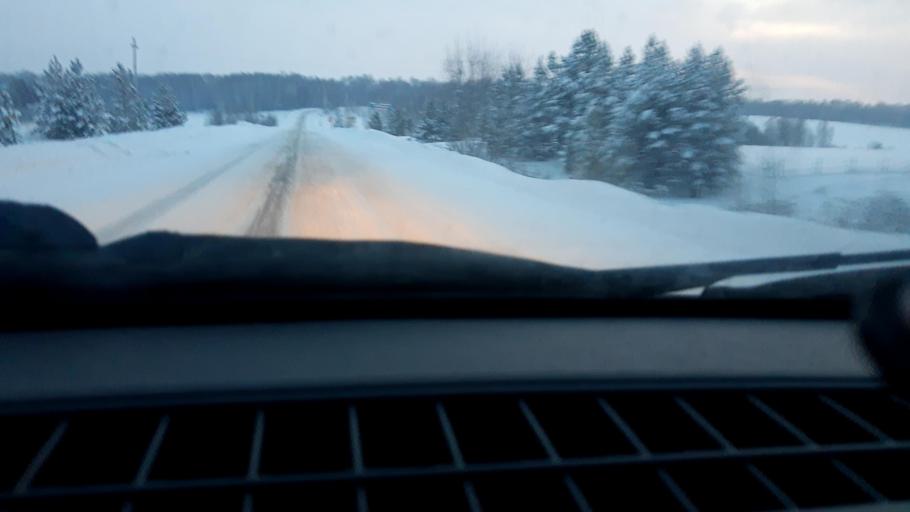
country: RU
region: Bashkortostan
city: Davlekanovo
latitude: 54.5677
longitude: 54.9557
